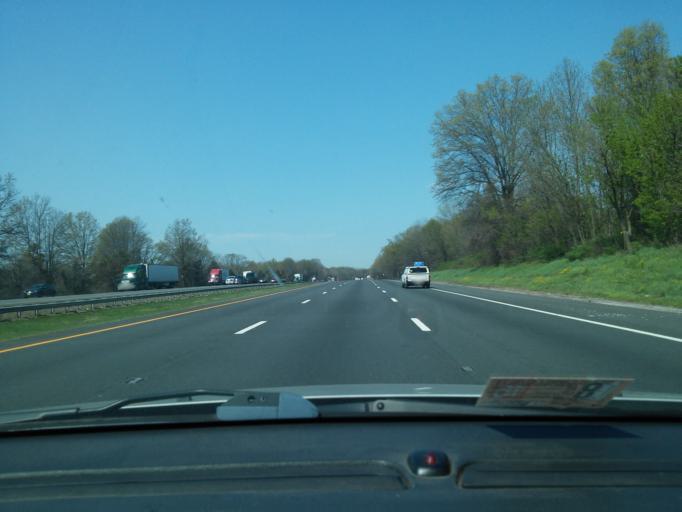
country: US
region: New Jersey
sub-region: Somerset County
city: Bedminster
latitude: 40.6440
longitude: -74.6694
